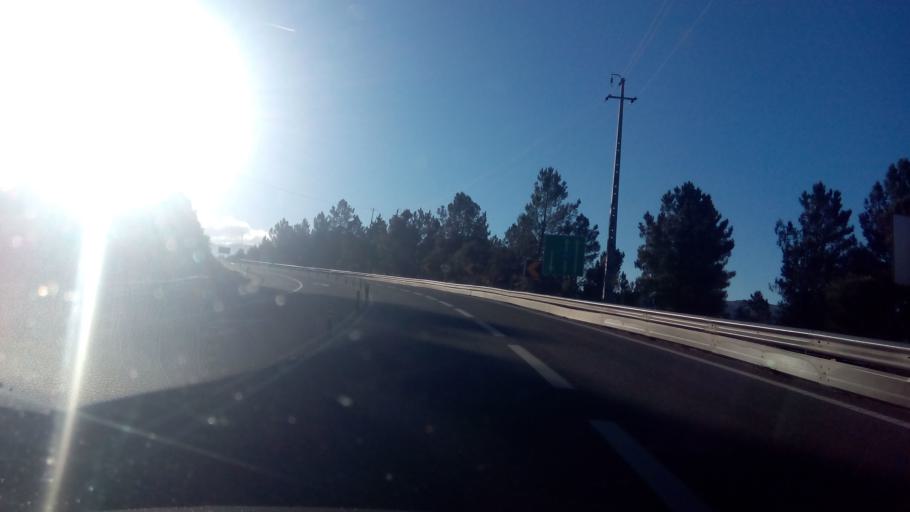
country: PT
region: Porto
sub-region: Baiao
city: Valadares
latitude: 41.2572
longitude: -7.9693
